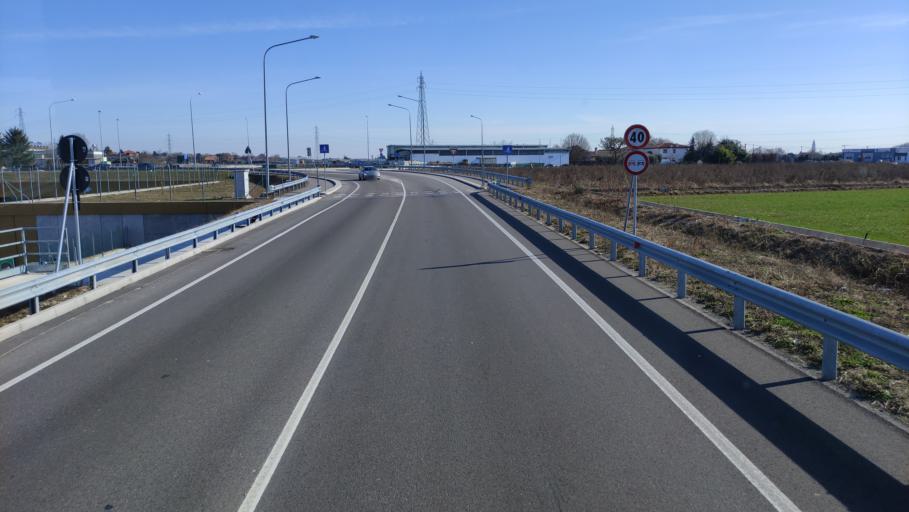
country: IT
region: Veneto
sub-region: Provincia di Vicenza
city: Bassano del Grappa
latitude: 45.7361
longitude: 11.7399
